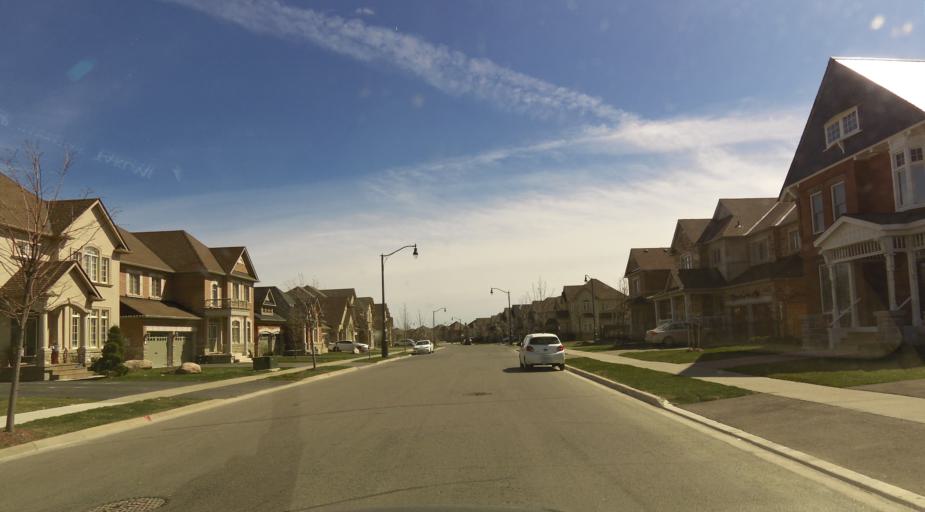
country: CA
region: Ontario
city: Brampton
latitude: 43.6574
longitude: -79.8107
